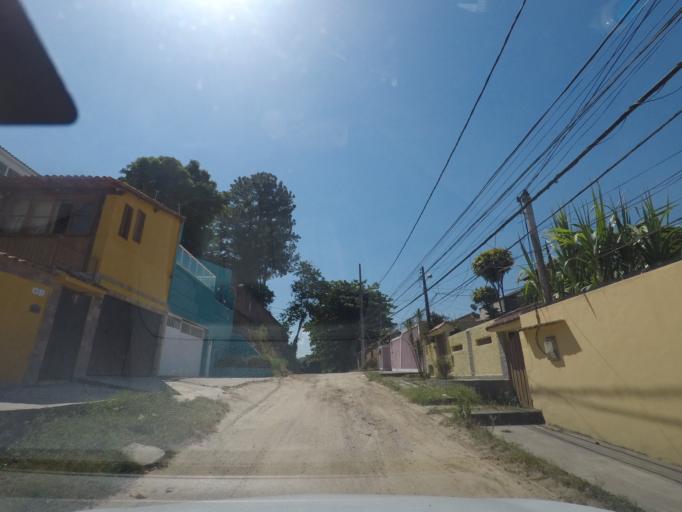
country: BR
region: Rio de Janeiro
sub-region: Niteroi
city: Niteroi
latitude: -22.9449
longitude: -43.0269
